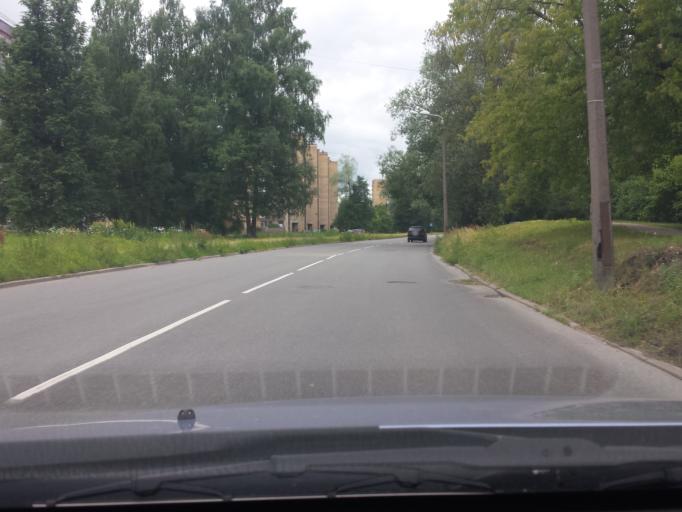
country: LV
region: Riga
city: Jaunciems
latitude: 56.9654
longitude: 24.1900
